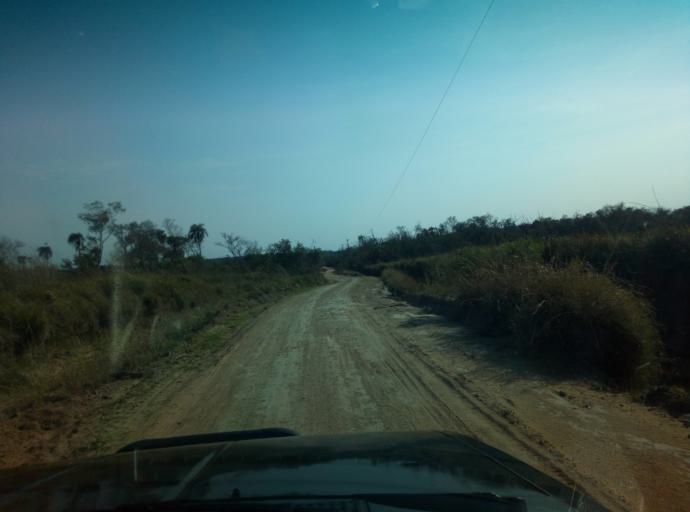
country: PY
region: Caaguazu
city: Doctor Cecilio Baez
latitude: -25.1904
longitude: -56.1917
